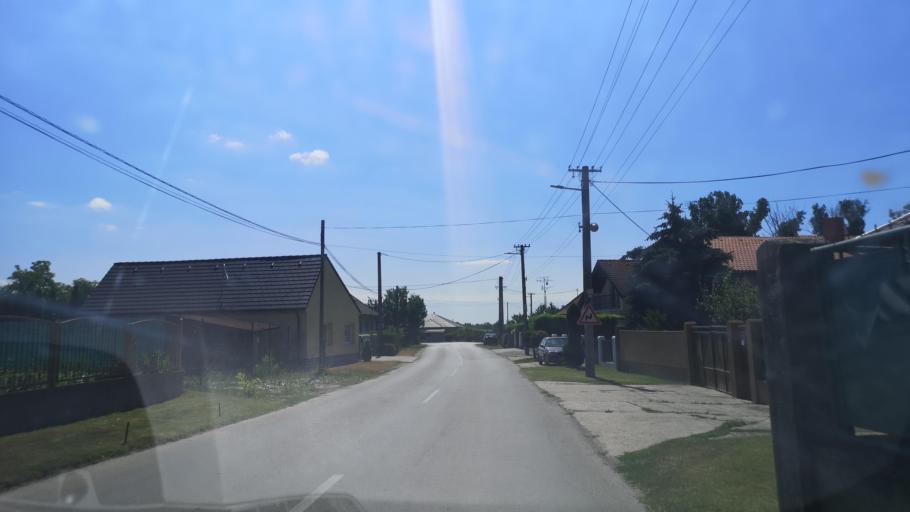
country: SK
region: Bratislavsky
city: Senec
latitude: 48.1002
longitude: 17.4777
